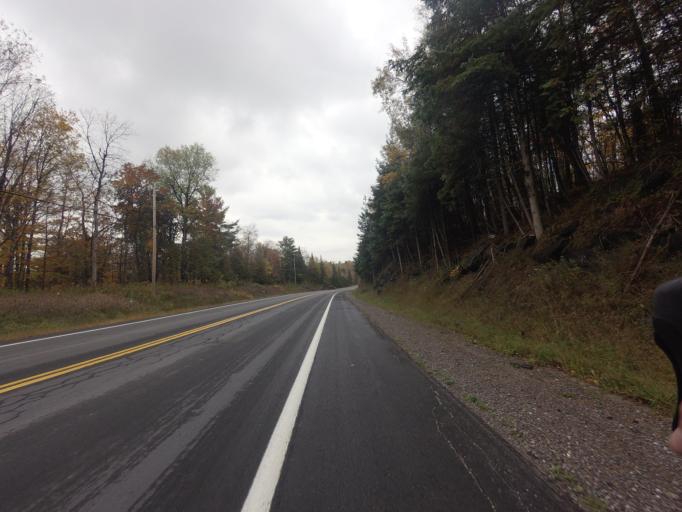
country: CA
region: Ontario
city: Perth
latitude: 45.1137
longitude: -76.4854
